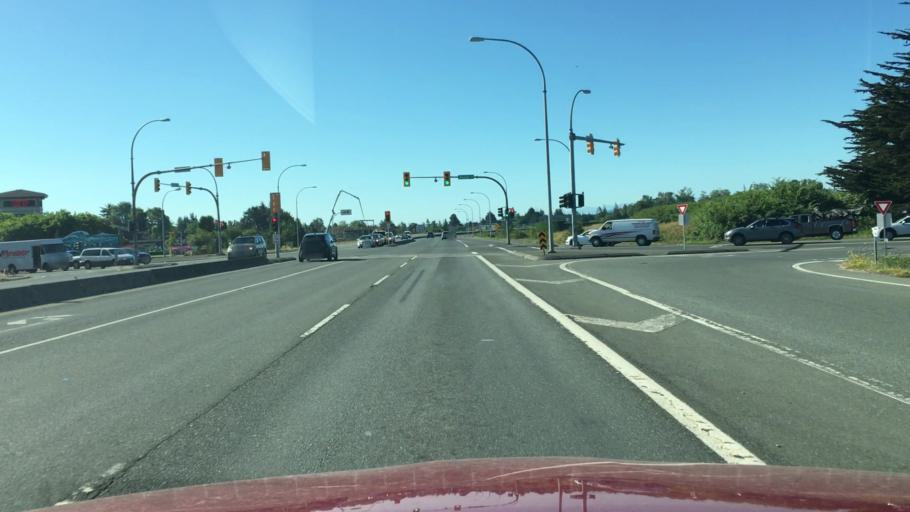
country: CA
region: British Columbia
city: North Saanich
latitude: 48.6494
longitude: -123.4076
